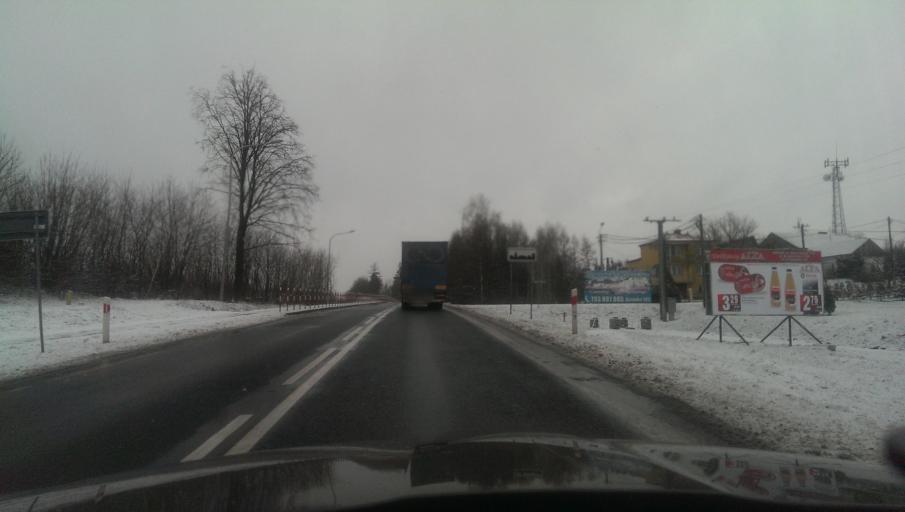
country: PL
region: Subcarpathian Voivodeship
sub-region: Powiat sanocki
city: Nowosielce-Gniewosz
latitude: 49.5731
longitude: 22.0607
